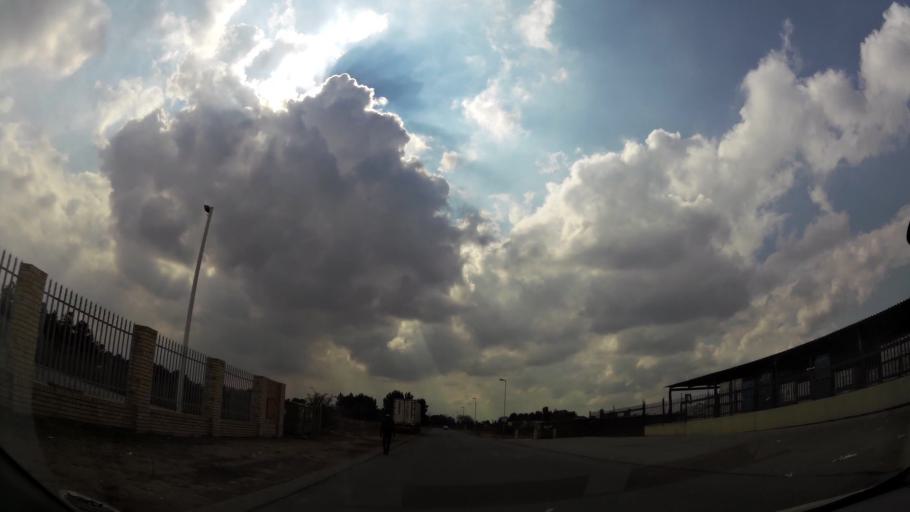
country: ZA
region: Gauteng
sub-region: Sedibeng District Municipality
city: Vereeniging
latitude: -26.6578
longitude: 27.9334
